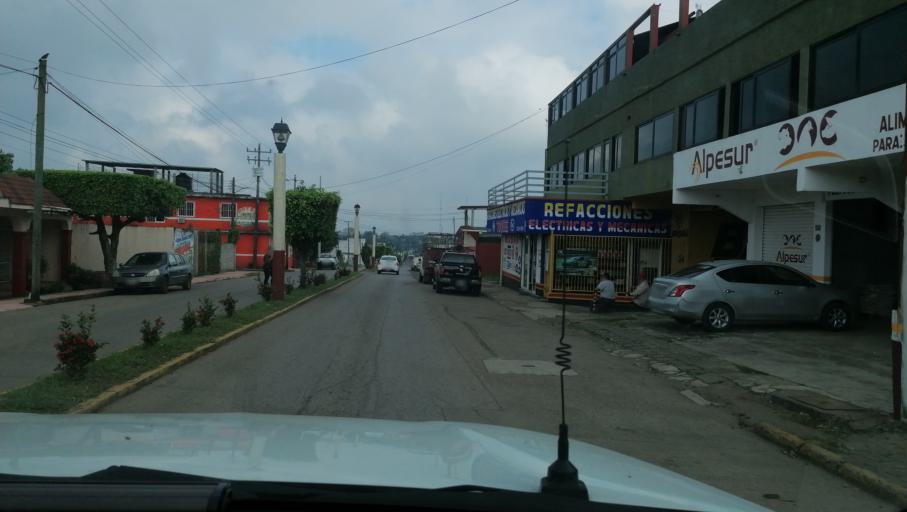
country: MX
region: Chiapas
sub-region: Juarez
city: El Triunfo 1ra. Seccion (Cardona)
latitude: 17.6052
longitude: -93.1895
